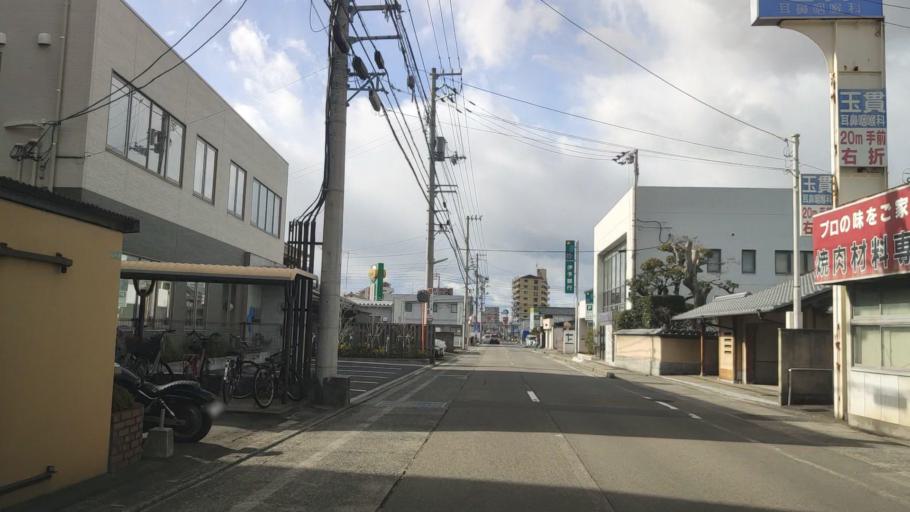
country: JP
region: Ehime
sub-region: Shikoku-chuo Shi
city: Matsuyama
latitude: 33.8092
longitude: 132.7819
